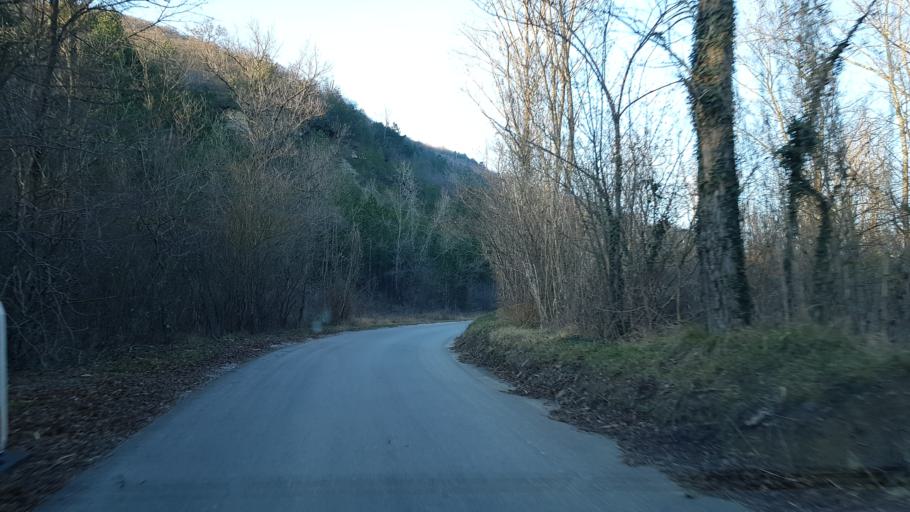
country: SI
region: Koper-Capodistria
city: Prade
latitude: 45.4855
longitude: 13.7750
